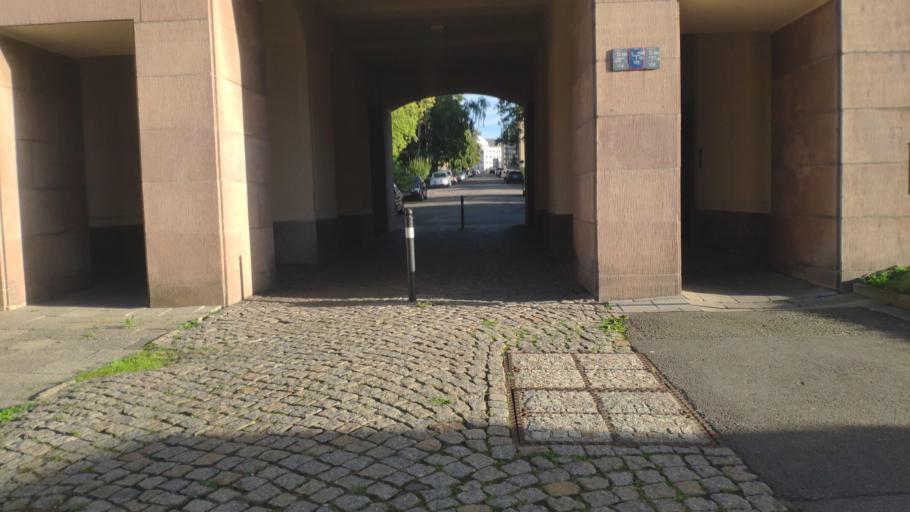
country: DE
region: Saxony
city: Chemnitz
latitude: 50.8264
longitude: 12.9380
